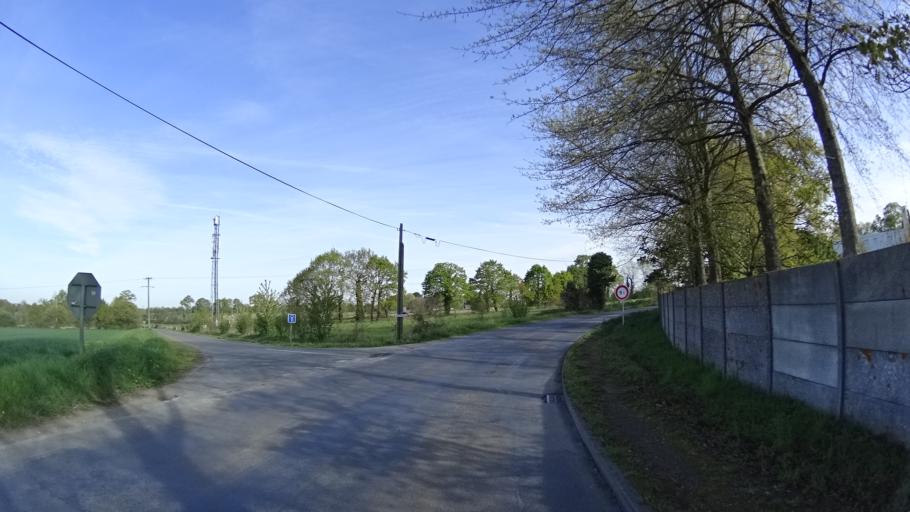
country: FR
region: Brittany
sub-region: Departement d'Ille-et-Vilaine
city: Vezin-le-Coquet
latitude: 48.1075
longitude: -1.7441
